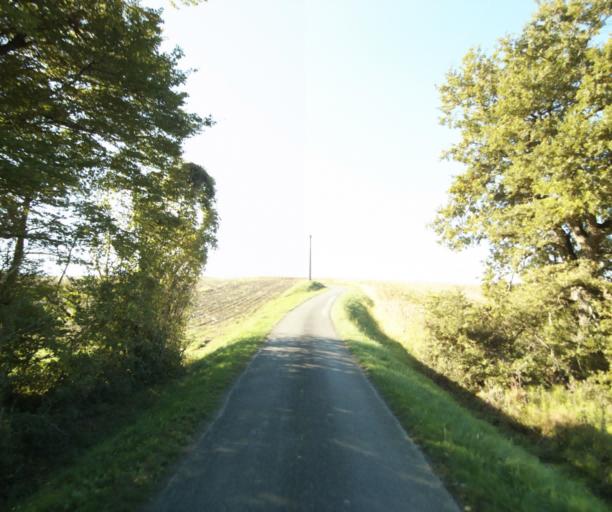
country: FR
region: Midi-Pyrenees
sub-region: Departement du Gers
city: Eauze
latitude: 43.8077
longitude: 0.1549
